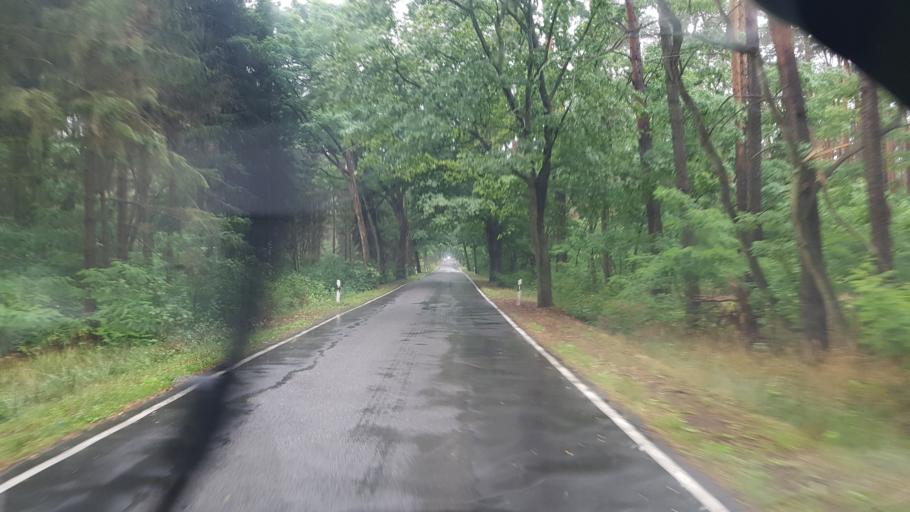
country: DE
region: Brandenburg
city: Dahme
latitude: 51.9336
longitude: 13.3969
